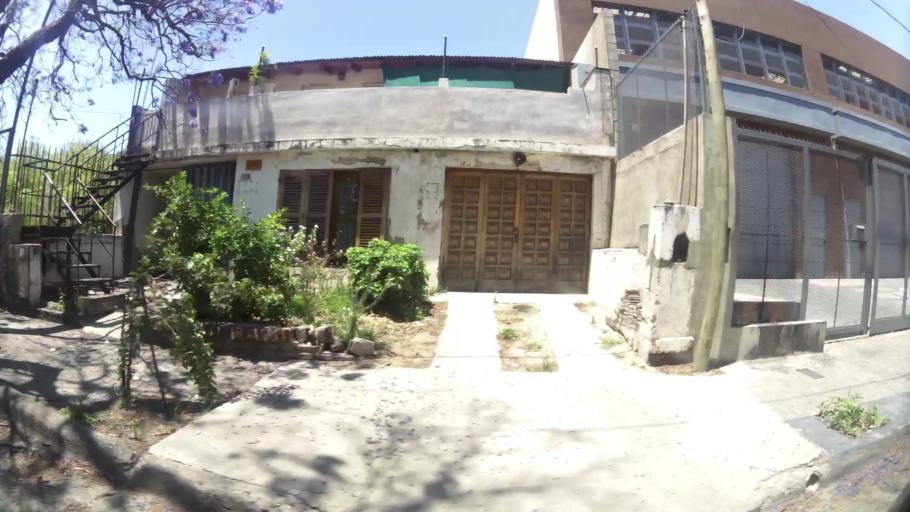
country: AR
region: Cordoba
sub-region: Departamento de Capital
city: Cordoba
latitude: -31.3977
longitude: -64.2021
